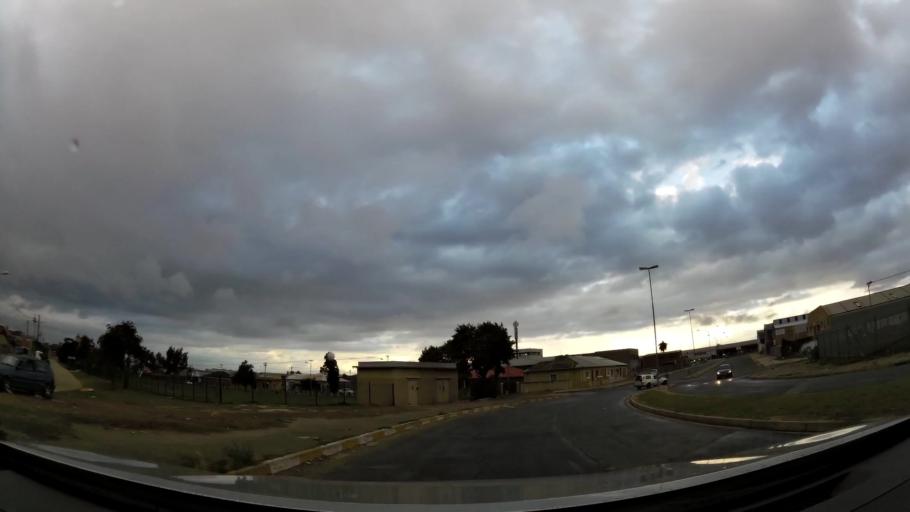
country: ZA
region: Eastern Cape
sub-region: Nelson Mandela Bay Metropolitan Municipality
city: Port Elizabeth
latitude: -33.9186
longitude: 25.5966
